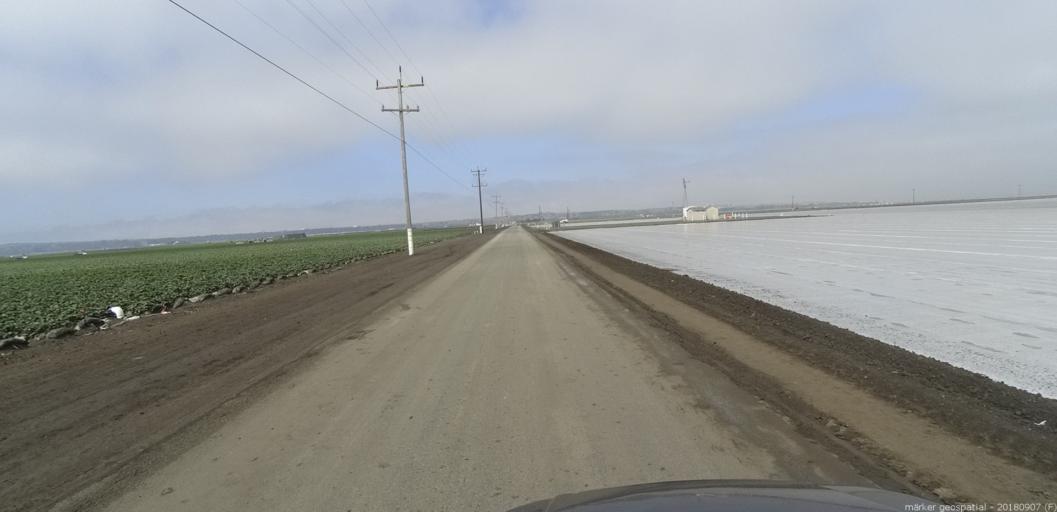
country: US
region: California
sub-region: Monterey County
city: Boronda
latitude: 36.6933
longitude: -121.7222
